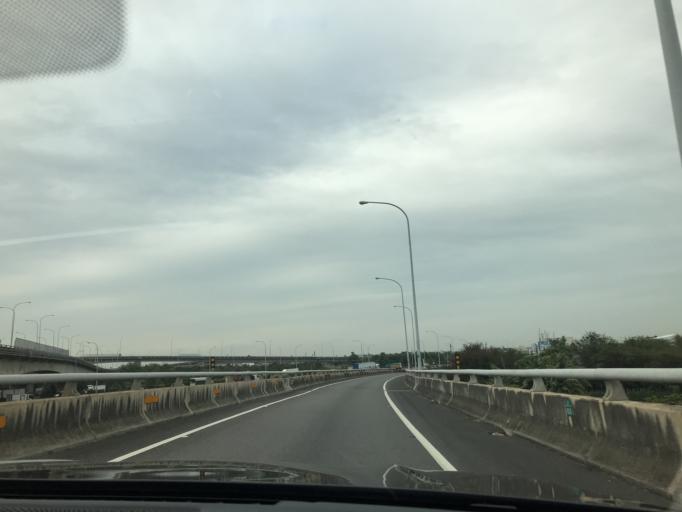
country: TW
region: Taiwan
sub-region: Changhua
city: Chang-hua
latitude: 23.9835
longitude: 120.5088
